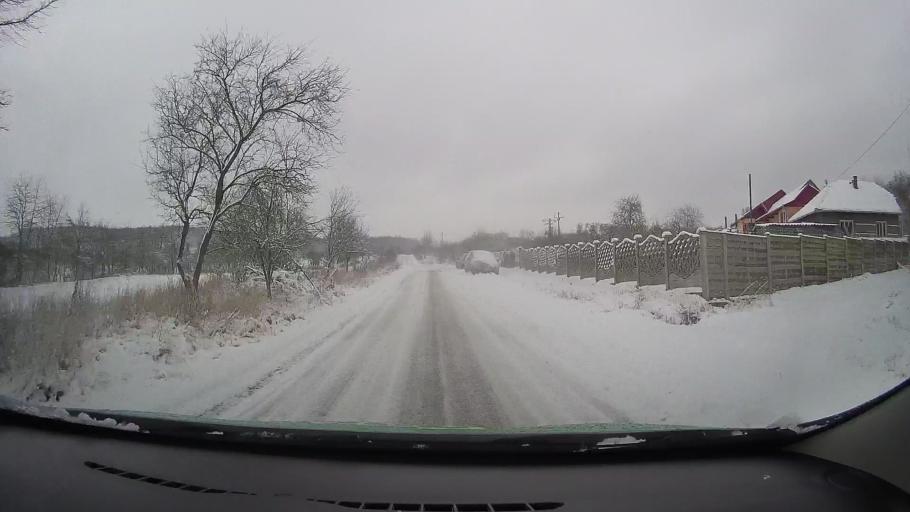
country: RO
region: Hunedoara
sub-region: Comuna Pestisu Mic
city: Pestisu Mic
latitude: 45.8167
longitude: 22.8939
